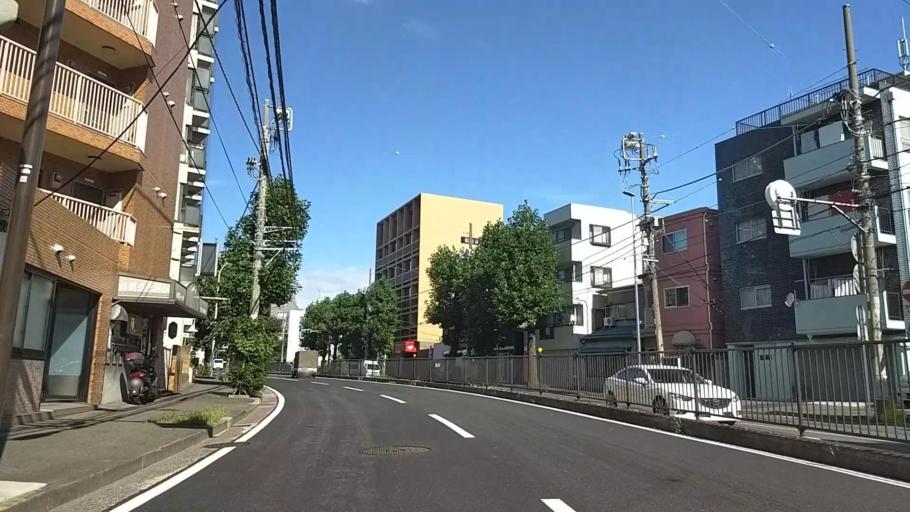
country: JP
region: Kanagawa
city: Yokohama
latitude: 35.4893
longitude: 139.6233
